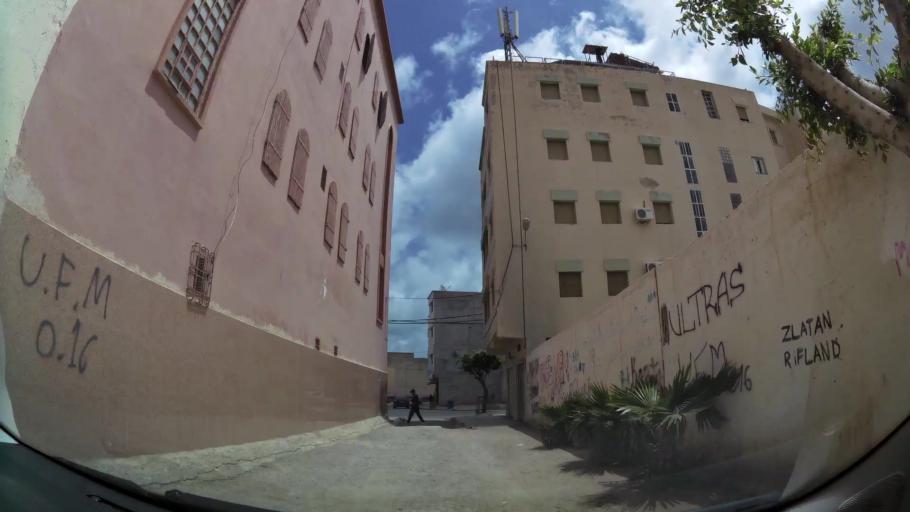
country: MA
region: Oriental
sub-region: Nador
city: Nador
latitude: 35.1731
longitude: -2.9187
